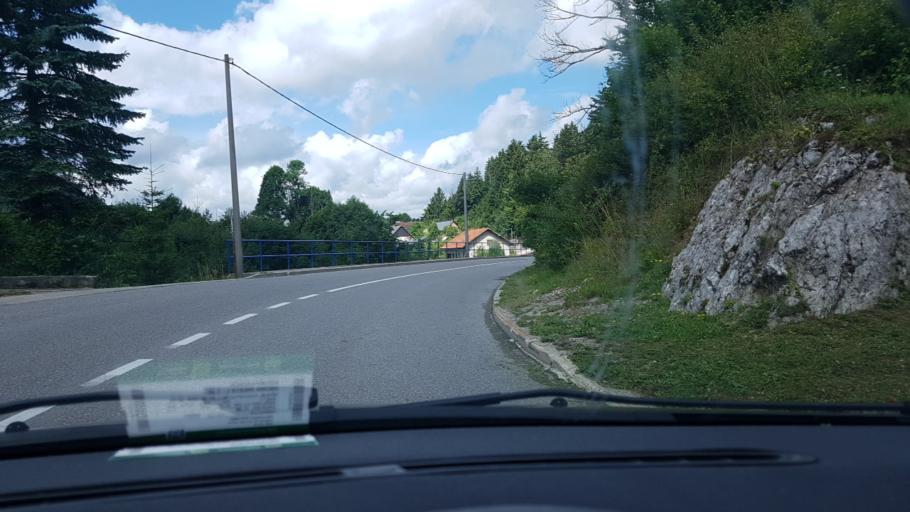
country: HR
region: Primorsko-Goranska
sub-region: Grad Delnice
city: Delnice
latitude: 45.3563
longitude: 14.7414
